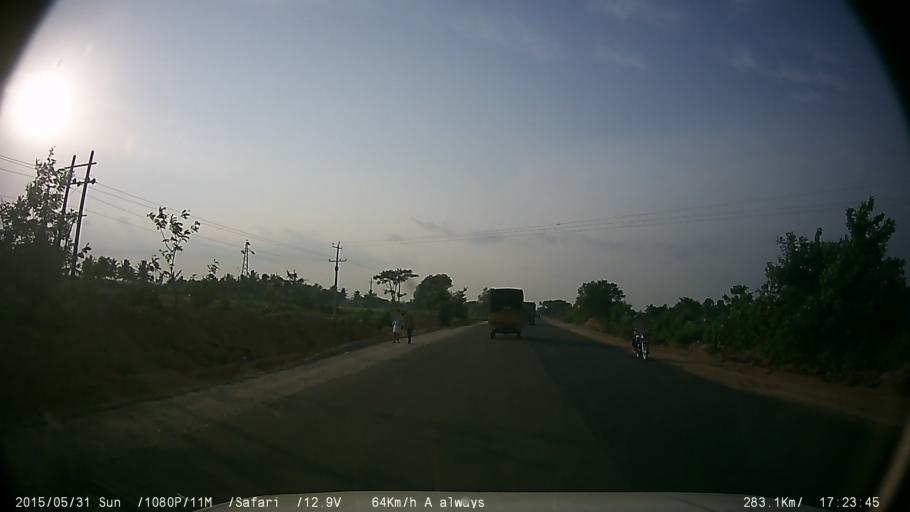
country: IN
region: Karnataka
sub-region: Chamrajnagar
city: Gundlupet
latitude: 11.8428
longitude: 76.6732
